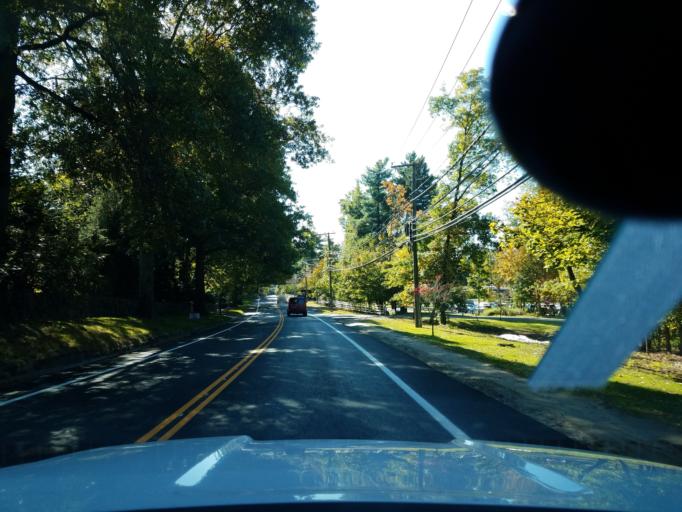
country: US
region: Connecticut
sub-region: Fairfield County
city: Cos Cob
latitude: 41.0599
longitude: -73.6183
